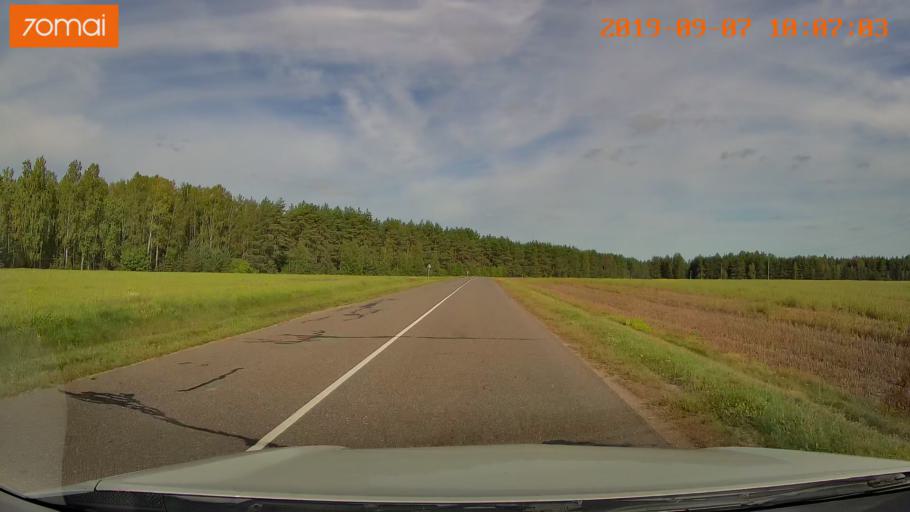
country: BY
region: Grodnenskaya
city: Voranava
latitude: 54.0699
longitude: 25.3968
